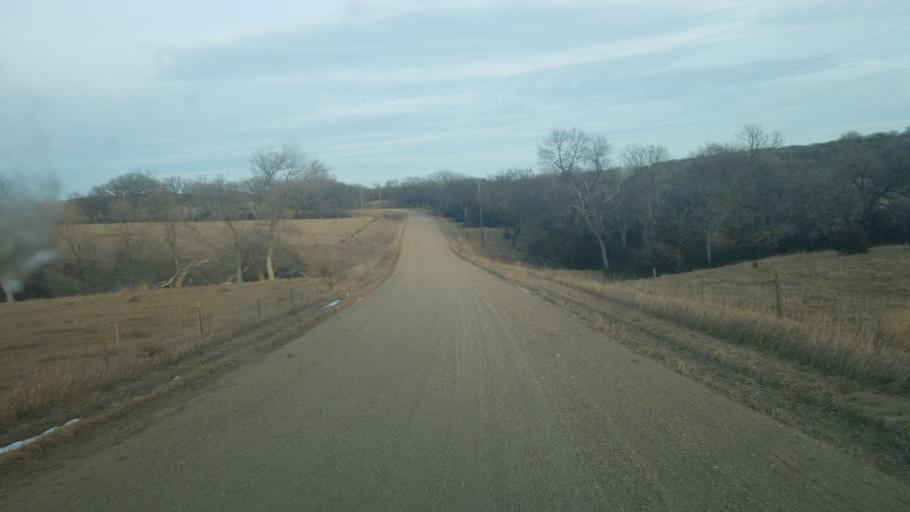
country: US
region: Nebraska
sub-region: Knox County
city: Center
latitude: 42.6922
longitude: -97.7974
